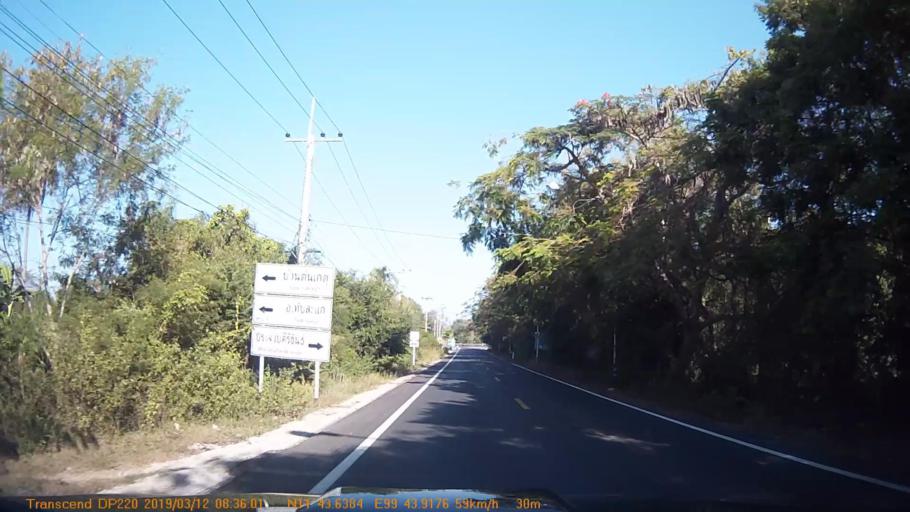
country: TH
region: Prachuap Khiri Khan
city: Prachuap Khiri Khan
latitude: 11.7275
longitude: 99.7317
